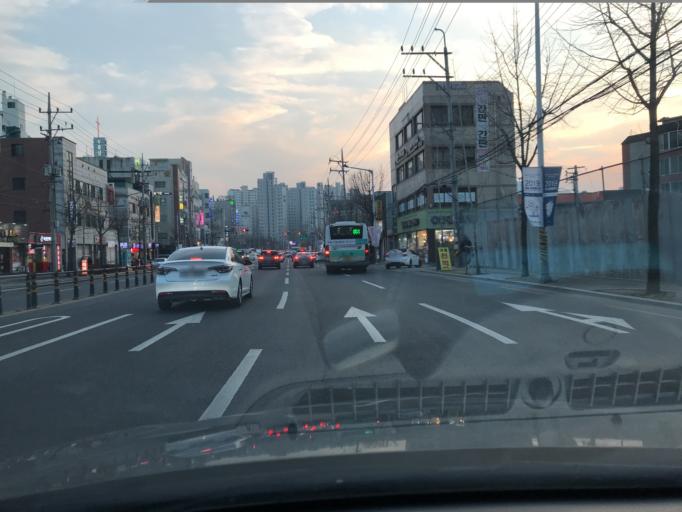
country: KR
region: Daegu
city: Hwawon
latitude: 35.8130
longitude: 128.5189
